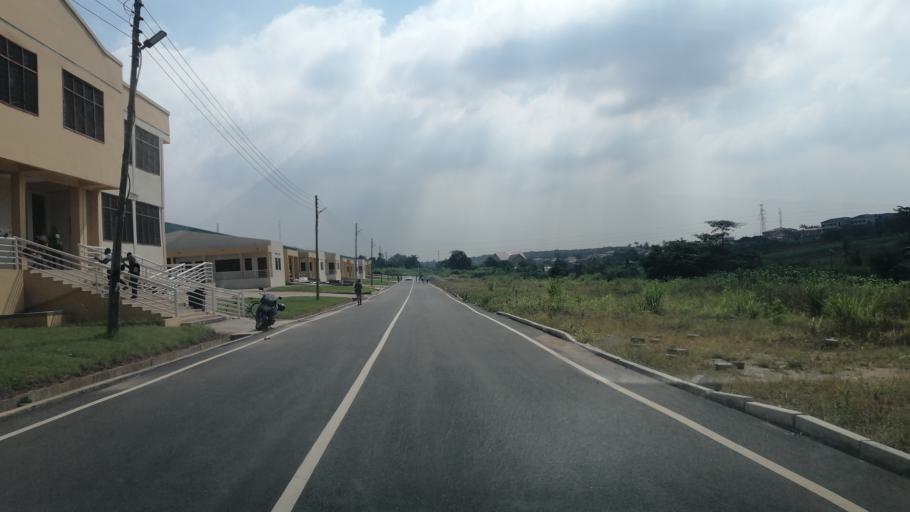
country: GH
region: Ashanti
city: Kumasi
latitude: 6.7000
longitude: -1.6808
